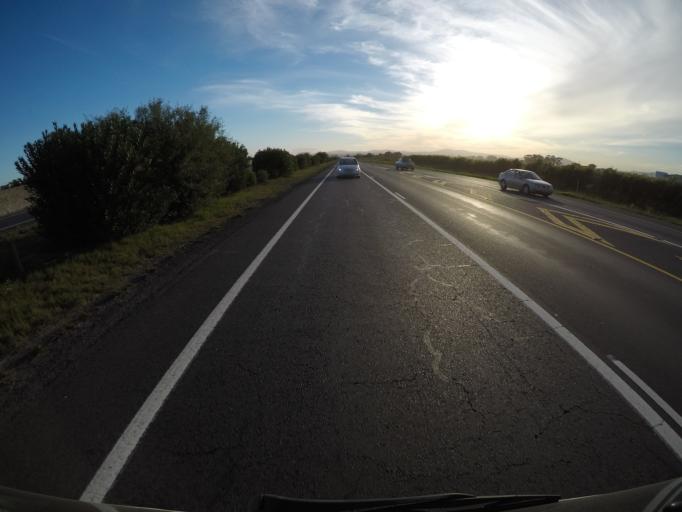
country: ZA
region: Western Cape
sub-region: City of Cape Town
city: Kraaifontein
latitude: -33.8286
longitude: 18.7600
